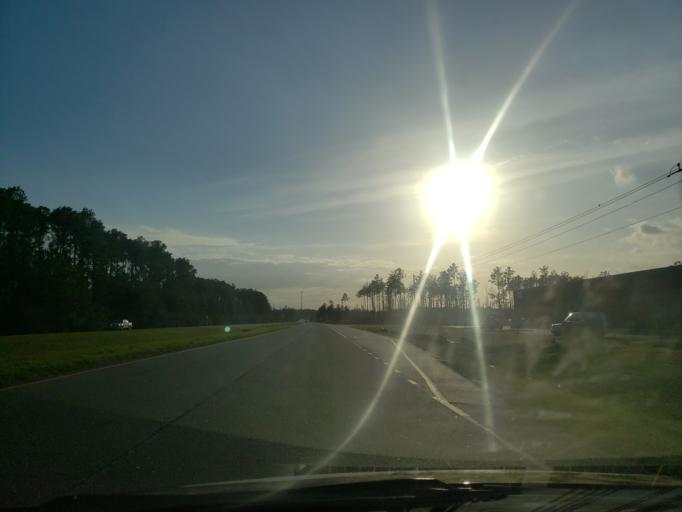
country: US
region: Georgia
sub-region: Chatham County
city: Bloomingdale
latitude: 32.1570
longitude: -81.2736
